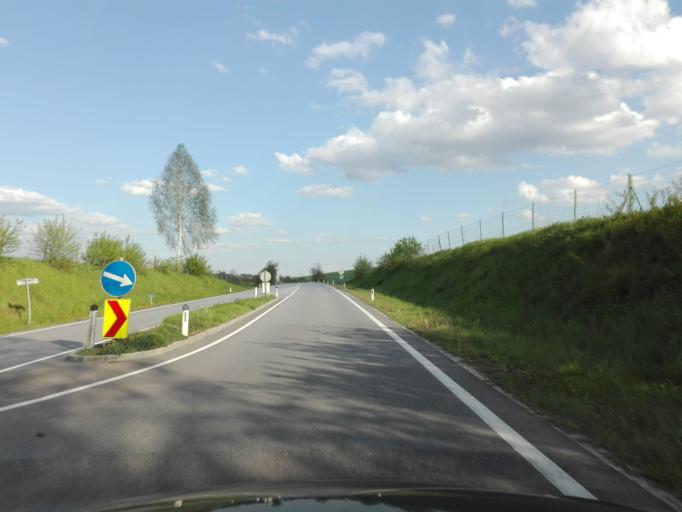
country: AT
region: Upper Austria
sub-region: Politischer Bezirk Rohrbach
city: Kleinzell im Muehlkreis
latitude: 48.4721
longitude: 14.0046
